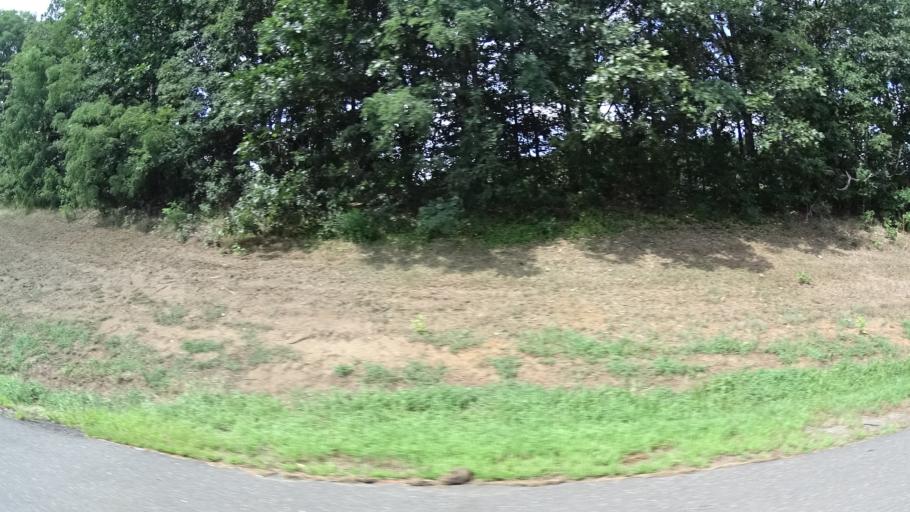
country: US
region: New Jersey
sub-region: Monmouth County
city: Tinton Falls
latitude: 40.3131
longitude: -74.0970
